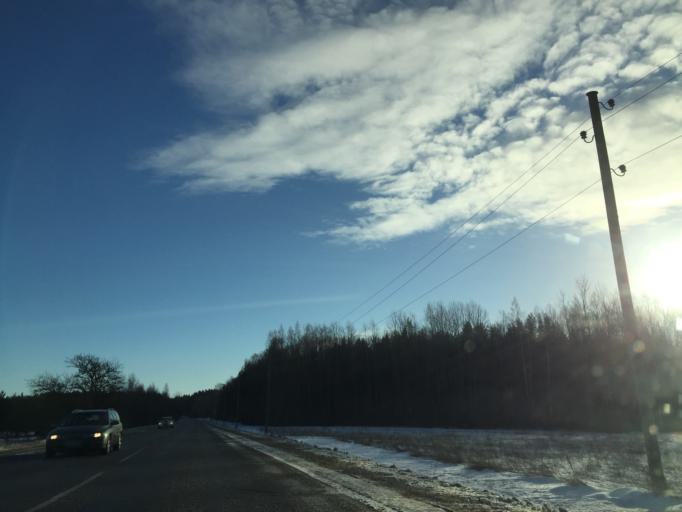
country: LV
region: Lielvarde
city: Lielvarde
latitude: 56.7072
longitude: 24.7762
